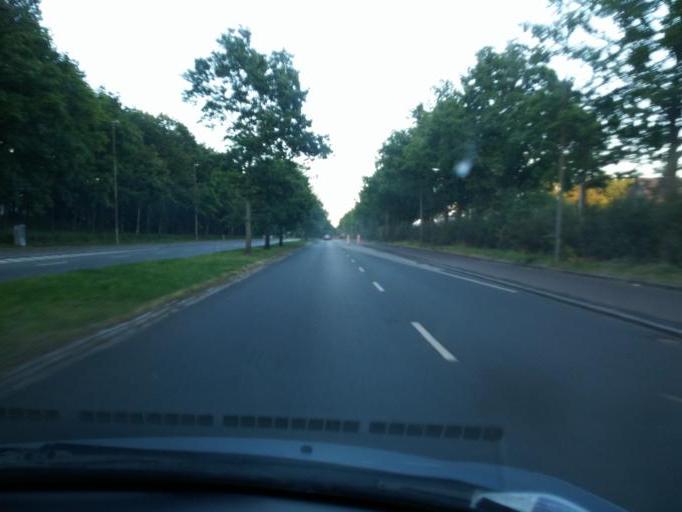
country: DK
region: South Denmark
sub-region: Odense Kommune
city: Seden
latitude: 55.4020
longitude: 10.4335
